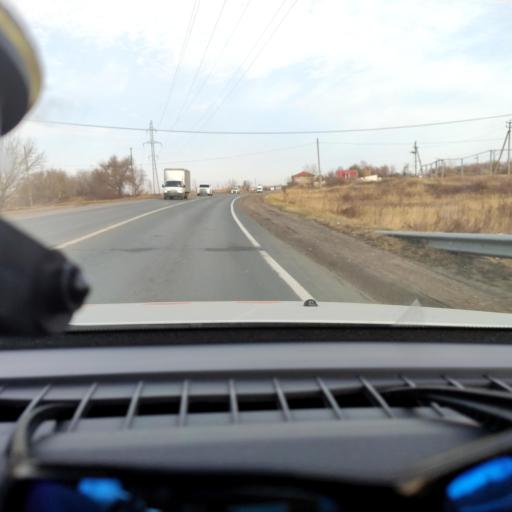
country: RU
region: Samara
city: Chapayevsk
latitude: 52.9920
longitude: 49.7671
